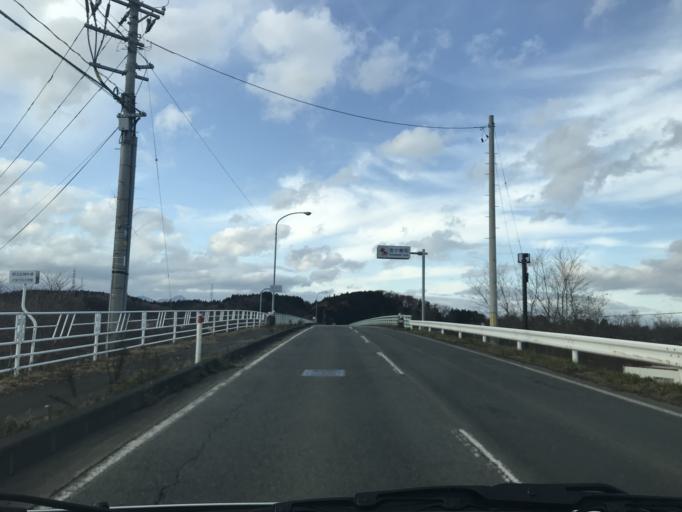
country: JP
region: Iwate
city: Mizusawa
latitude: 39.1650
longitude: 141.0913
